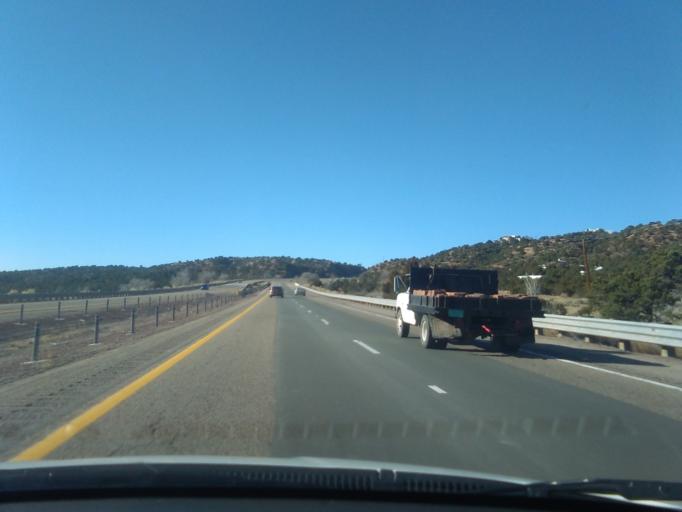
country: US
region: New Mexico
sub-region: Santa Fe County
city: Eldorado at Santa Fe
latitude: 35.5400
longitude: -105.8454
